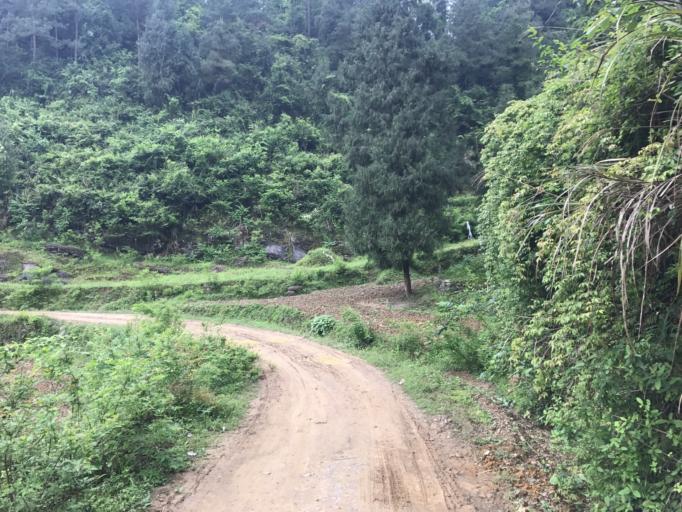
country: CN
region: Guizhou Sheng
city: Xujiaba
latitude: 27.7267
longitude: 108.0131
